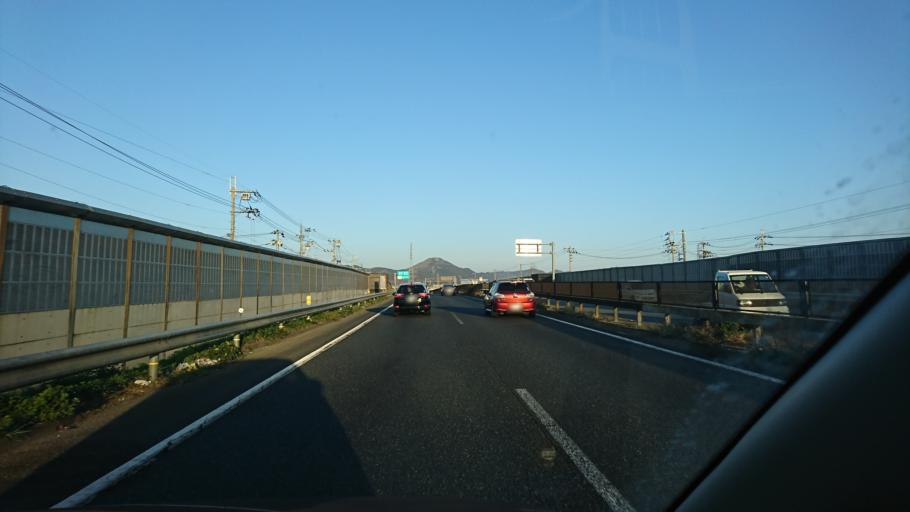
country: JP
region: Hyogo
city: Kakogawacho-honmachi
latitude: 34.7811
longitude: 134.8329
